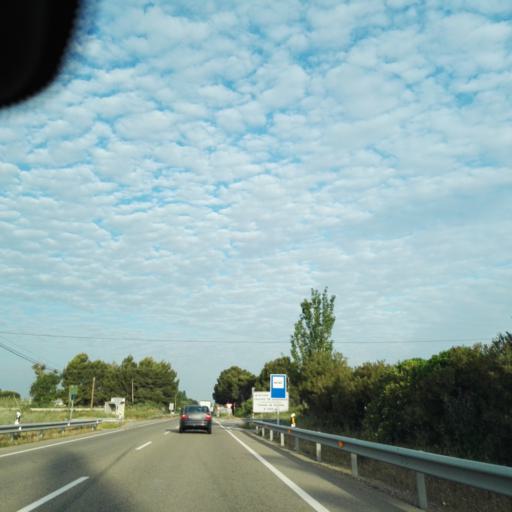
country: ES
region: Aragon
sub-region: Provincia de Zaragoza
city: Oliver-Valdefierro, Oliver, Valdefierro
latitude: 41.6636
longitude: -0.9800
